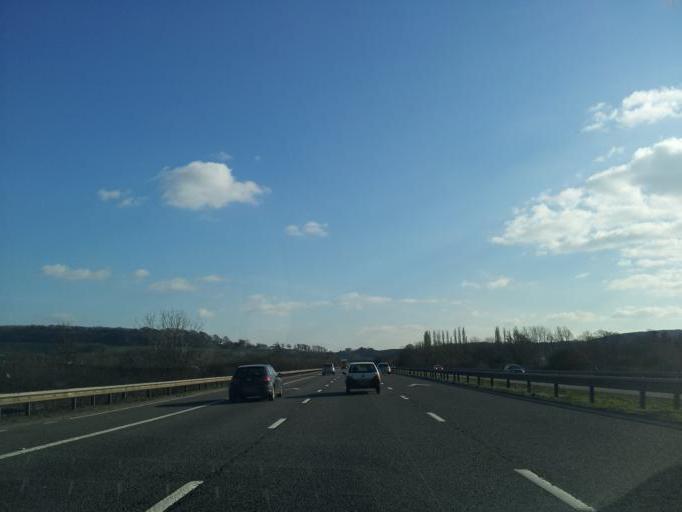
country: GB
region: England
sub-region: North Somerset
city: St. Georges
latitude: 51.3374
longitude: -2.8940
